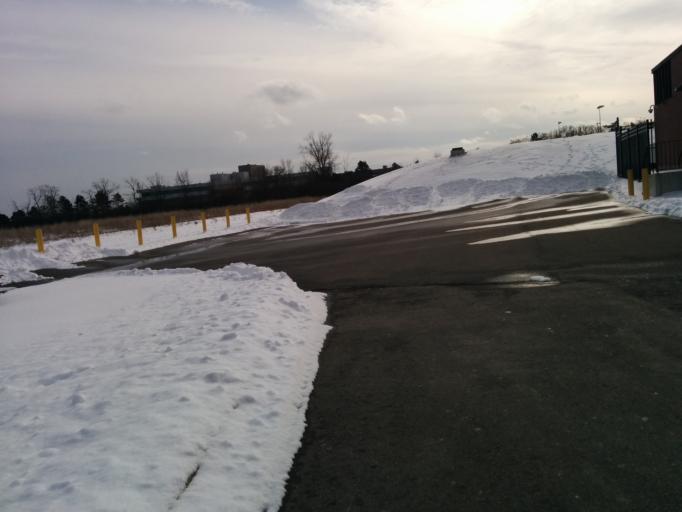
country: CA
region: Ontario
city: Mississauga
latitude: 43.5263
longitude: -79.6585
